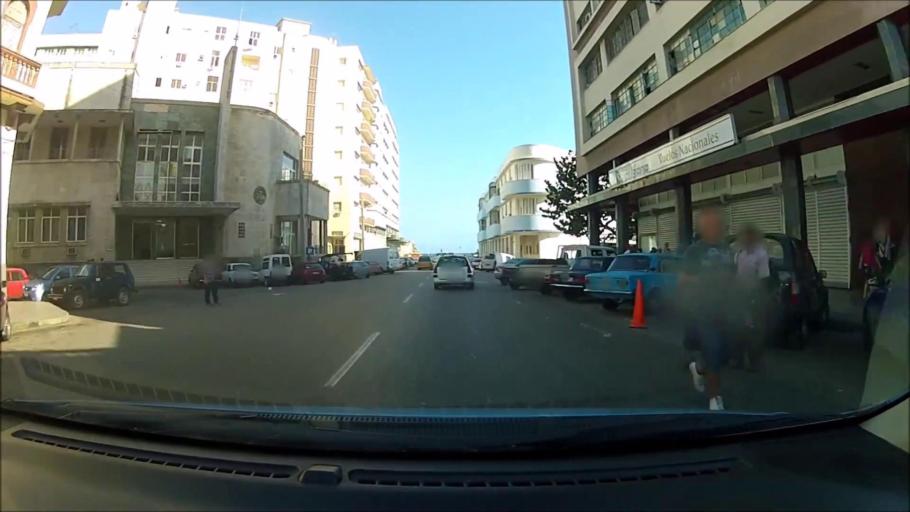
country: CU
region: La Habana
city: Havana
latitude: 23.1414
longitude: -82.3773
